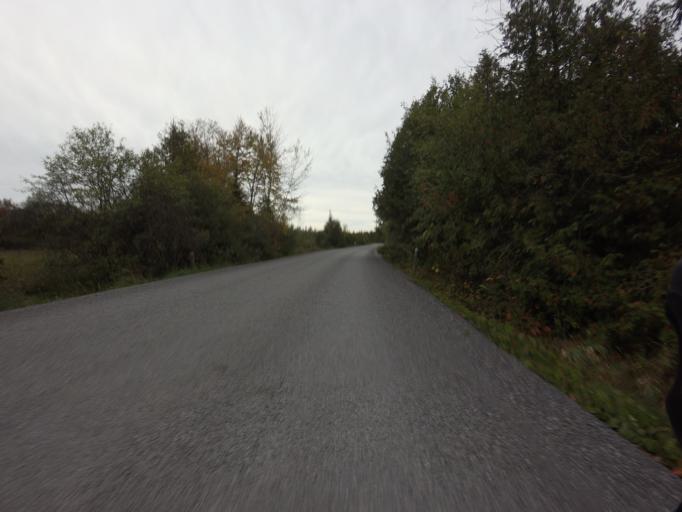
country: CA
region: Ontario
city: Bells Corners
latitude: 45.0840
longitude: -75.7571
